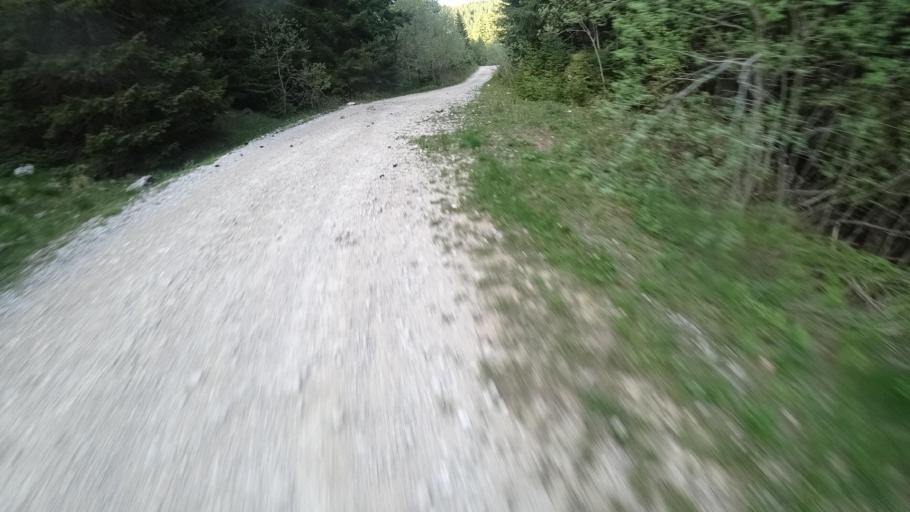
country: BA
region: Federation of Bosnia and Herzegovina
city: Rumboci
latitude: 43.7243
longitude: 17.5256
